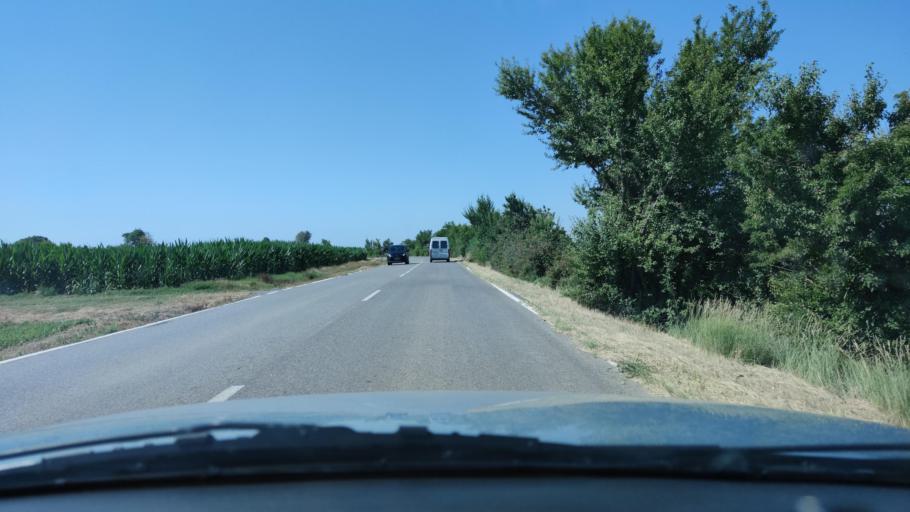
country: ES
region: Catalonia
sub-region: Provincia de Lleida
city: Castellsera
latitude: 41.7337
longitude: 0.9836
